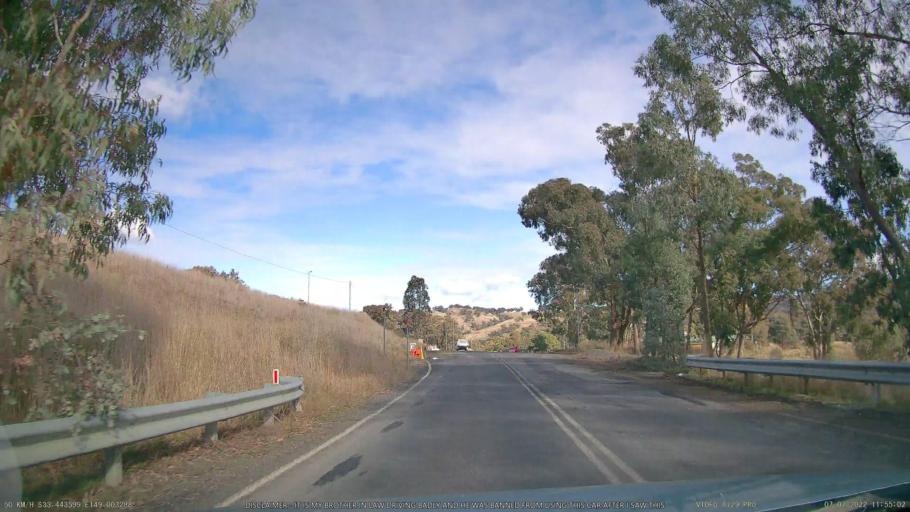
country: AU
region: New South Wales
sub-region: Blayney
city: Millthorpe
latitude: -33.4438
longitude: 149.0029
